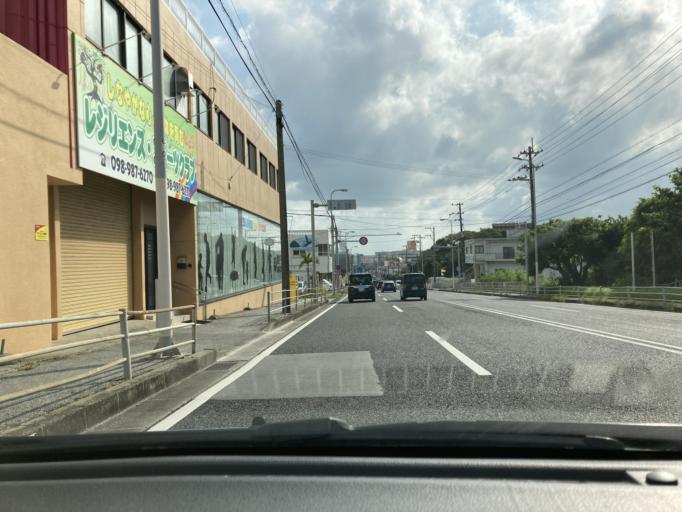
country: JP
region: Okinawa
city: Ginowan
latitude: 26.2301
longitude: 127.7684
